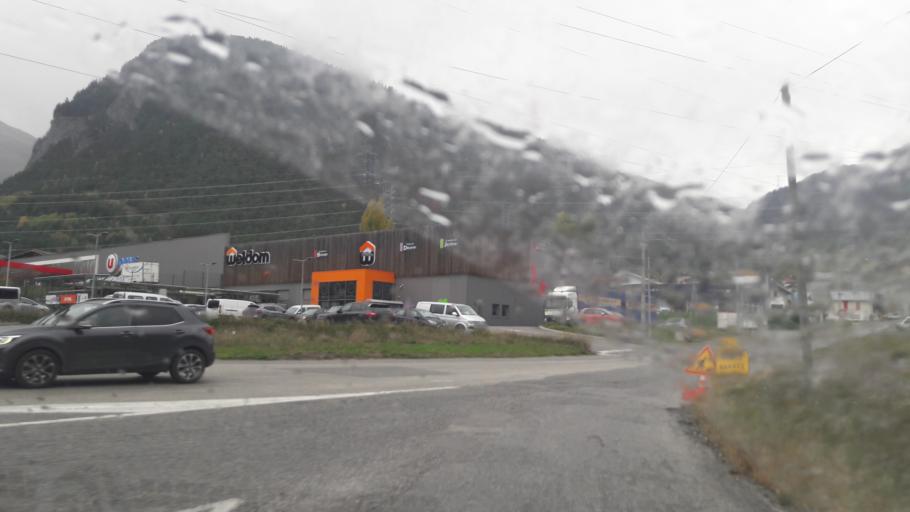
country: FR
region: Rhone-Alpes
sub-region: Departement de la Savoie
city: Seez
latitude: 45.6202
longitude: 6.7890
